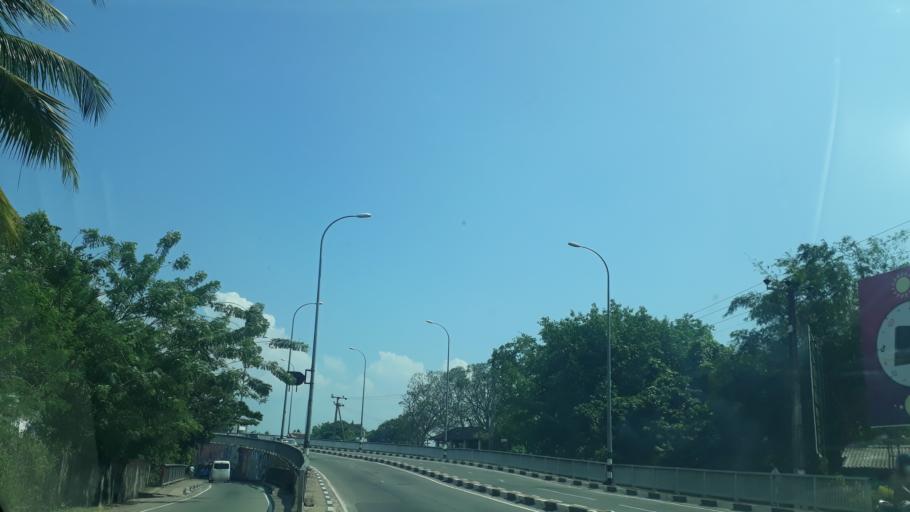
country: LK
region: Western
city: Gampaha
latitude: 7.0920
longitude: 79.9906
